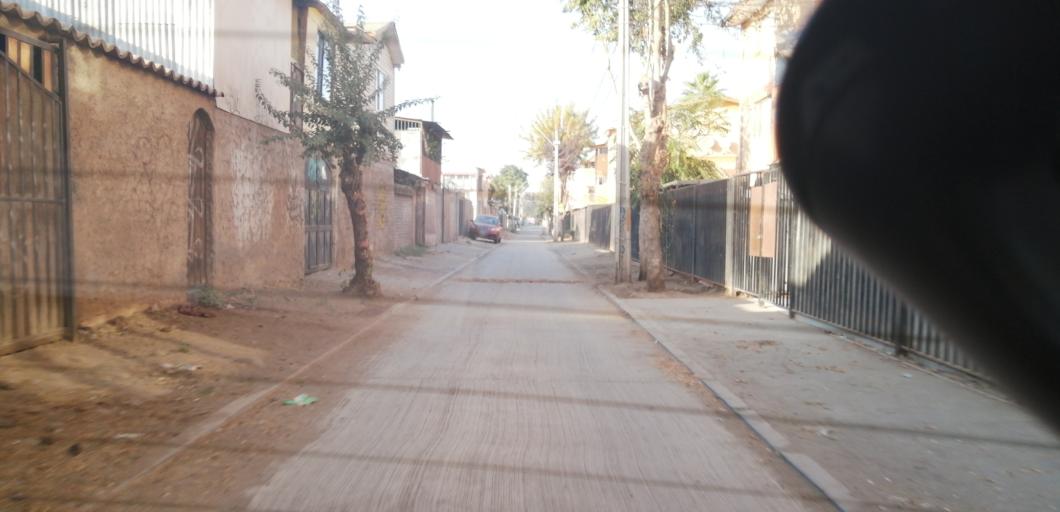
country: CL
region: Santiago Metropolitan
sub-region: Provincia de Santiago
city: Lo Prado
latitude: -33.4595
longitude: -70.7581
